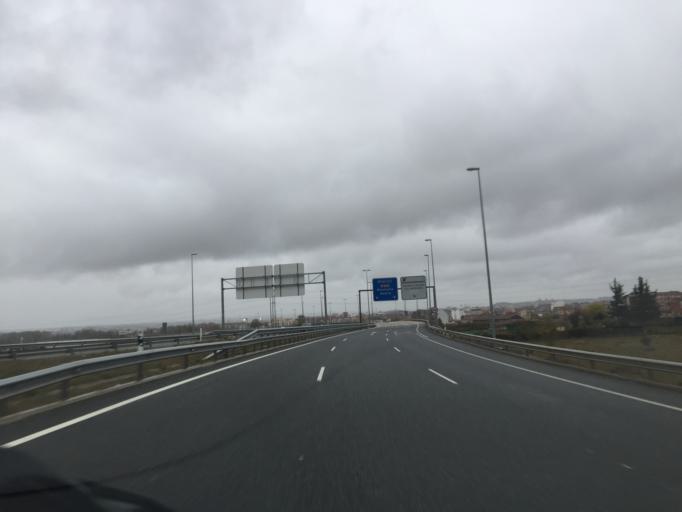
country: ES
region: Castille and Leon
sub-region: Provincia de Leon
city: Leon
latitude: 42.5725
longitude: -5.5486
